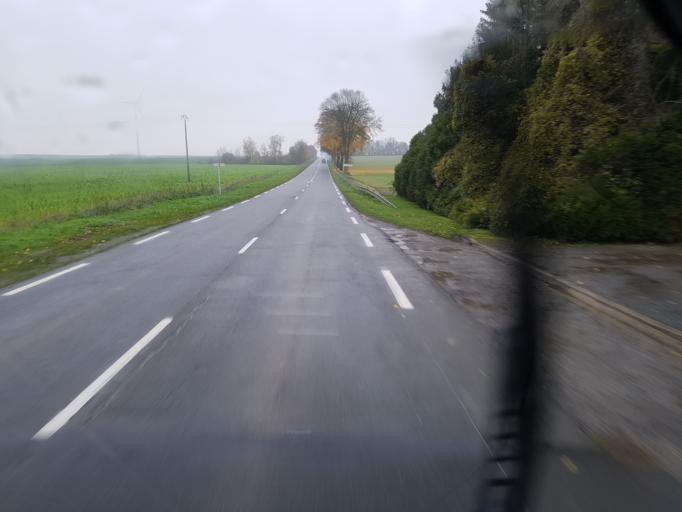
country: FR
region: Picardie
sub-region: Departement de l'Aisne
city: Saint-Quentin
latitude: 49.8941
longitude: 3.2640
